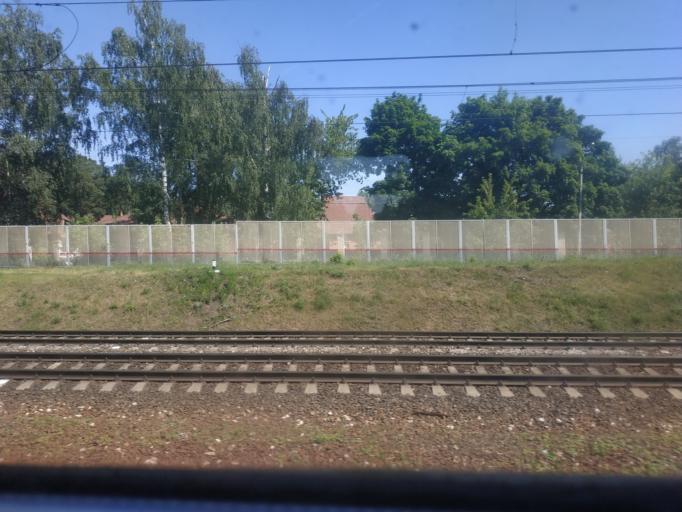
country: RU
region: Moskovskaya
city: Tomilino
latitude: 55.6539
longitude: 37.9607
